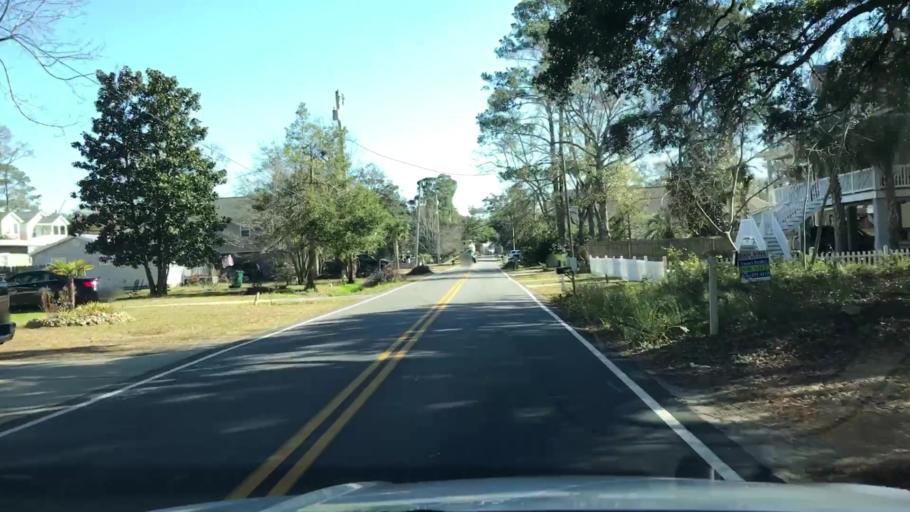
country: US
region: South Carolina
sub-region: Horry County
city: Garden City
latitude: 33.5924
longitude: -78.9992
